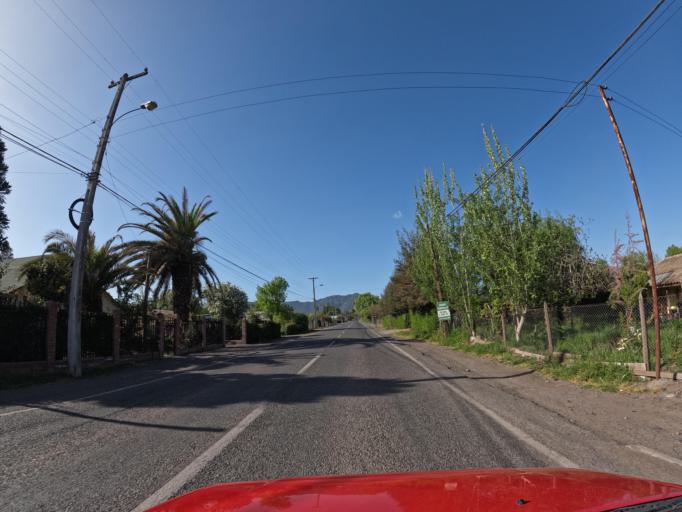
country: CL
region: Maule
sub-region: Provincia de Curico
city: Rauco
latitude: -34.8713
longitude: -71.2657
